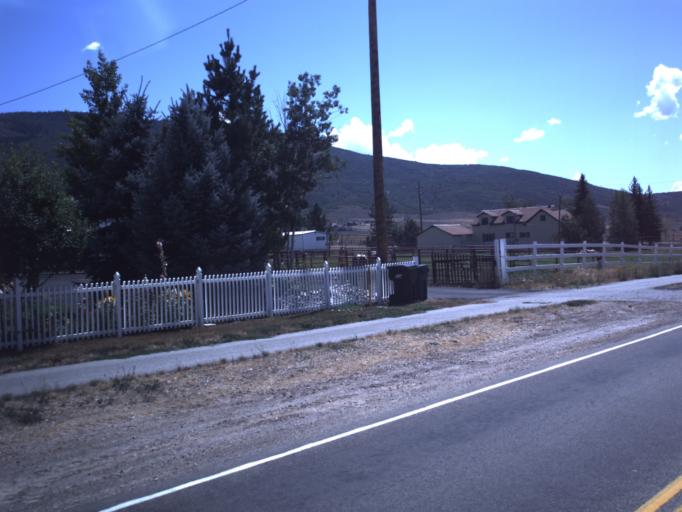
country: US
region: Utah
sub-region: Summit County
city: Oakley
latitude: 40.6852
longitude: -111.2810
